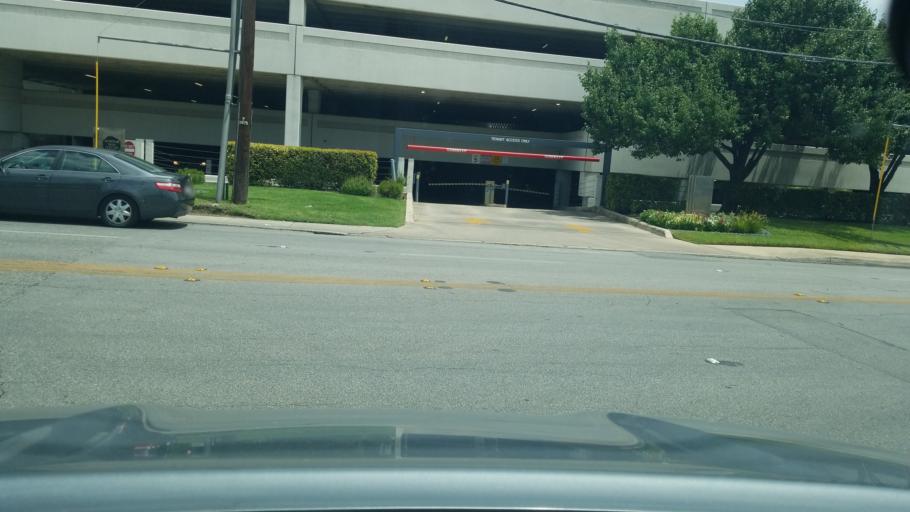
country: US
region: Texas
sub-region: Bexar County
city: Castle Hills
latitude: 29.5191
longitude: -98.4840
